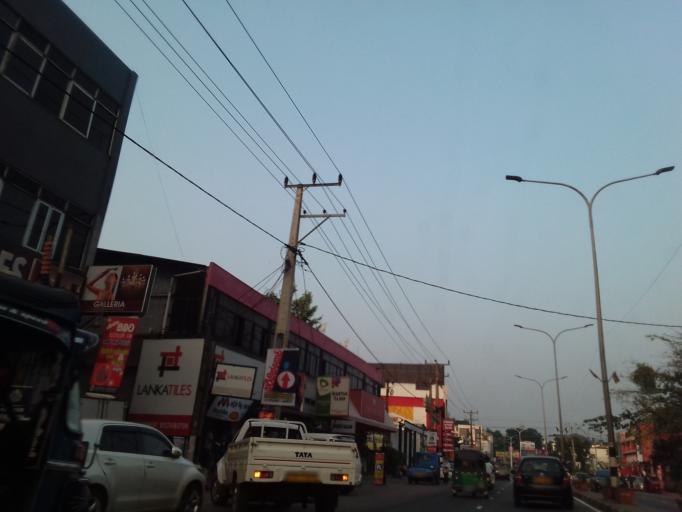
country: LK
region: Western
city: Kelaniya
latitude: 6.9847
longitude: 79.9336
